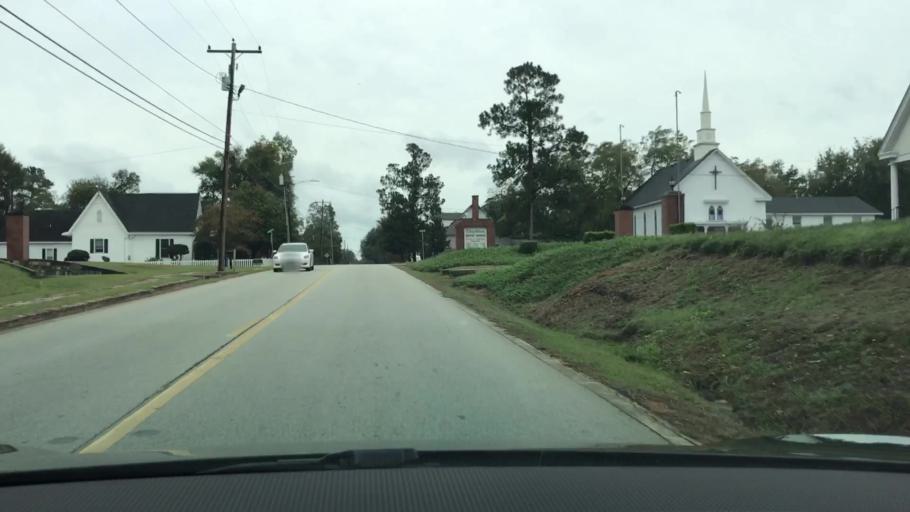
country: US
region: Georgia
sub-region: Jefferson County
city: Wrens
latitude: 33.2130
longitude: -82.4686
